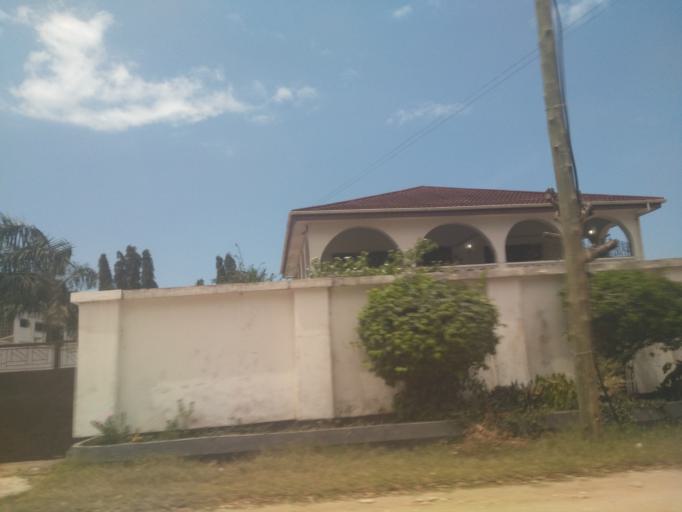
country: TZ
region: Dar es Salaam
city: Magomeni
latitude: -6.7539
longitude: 39.2813
